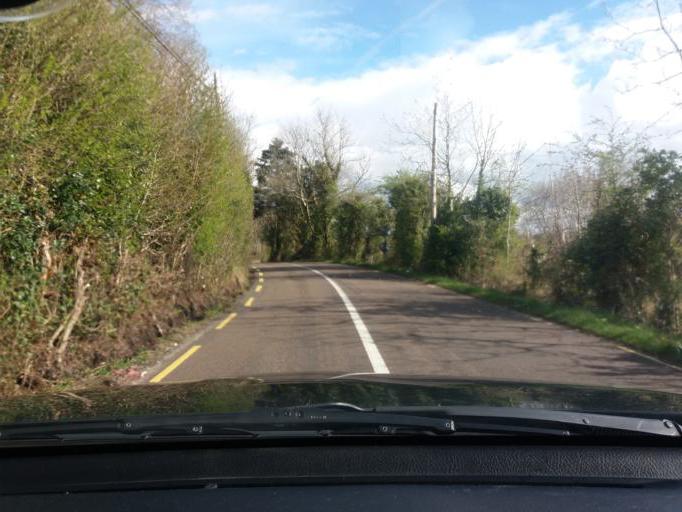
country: IE
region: Connaught
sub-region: County Leitrim
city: Kinlough
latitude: 54.3602
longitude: -8.2551
